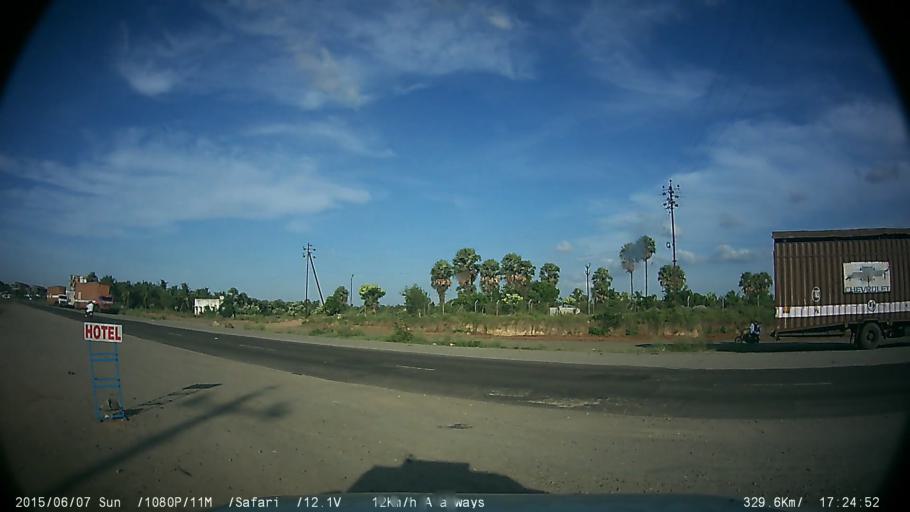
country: IN
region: Tamil Nadu
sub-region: Coimbatore
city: Madukkarai
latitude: 10.8702
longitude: 76.8864
